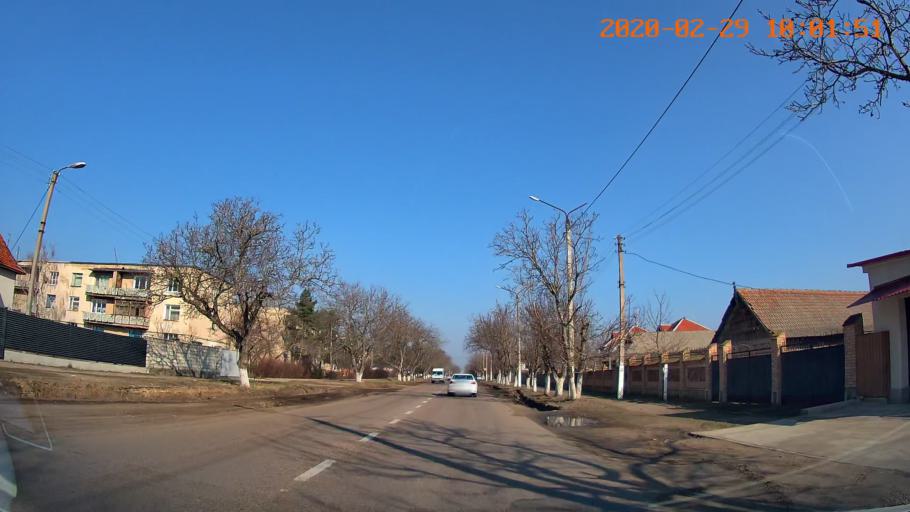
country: MD
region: Telenesti
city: Slobozia
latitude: 46.7782
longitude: 29.6843
